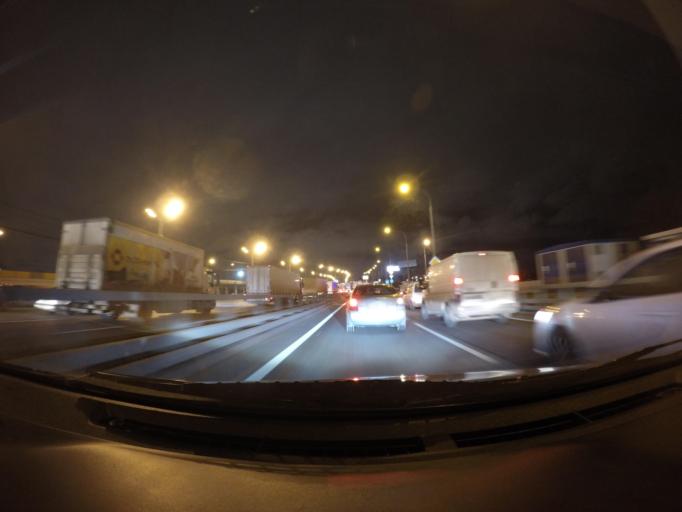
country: RU
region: Moskovskaya
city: Alekseyevka
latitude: 55.6194
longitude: 37.7850
